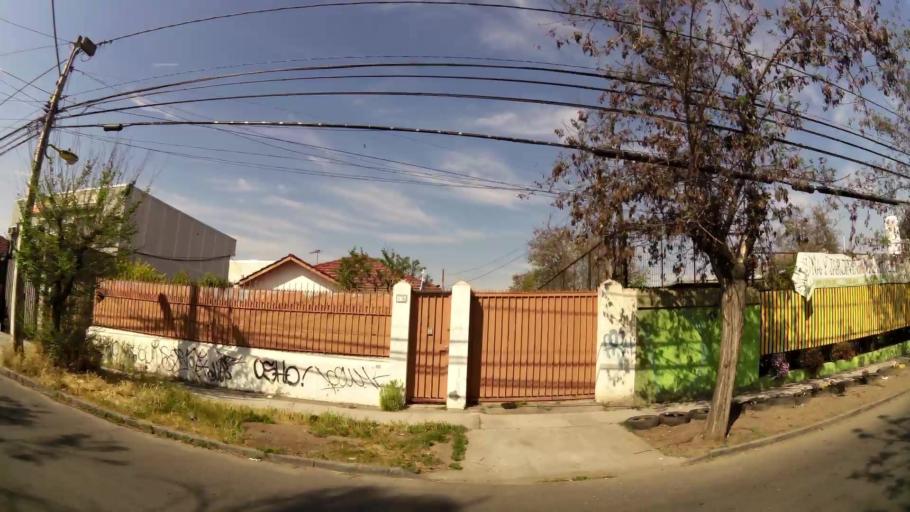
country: CL
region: Santiago Metropolitan
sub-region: Provincia de Maipo
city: San Bernardo
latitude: -33.5565
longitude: -70.6758
